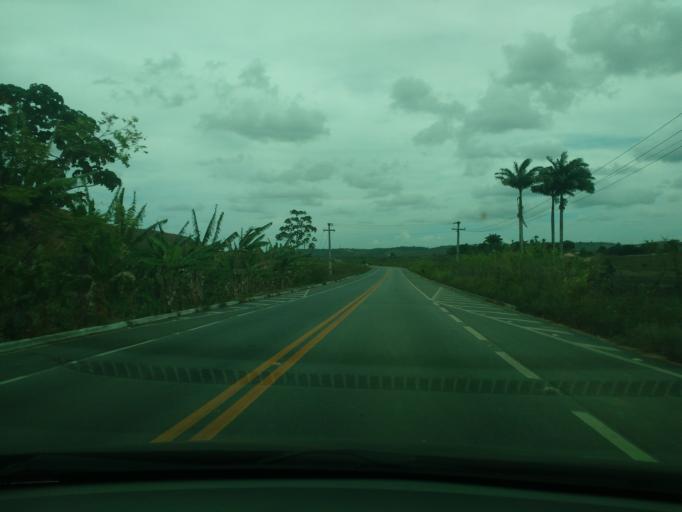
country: BR
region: Alagoas
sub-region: Murici
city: Murici
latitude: -9.2885
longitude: -35.9618
